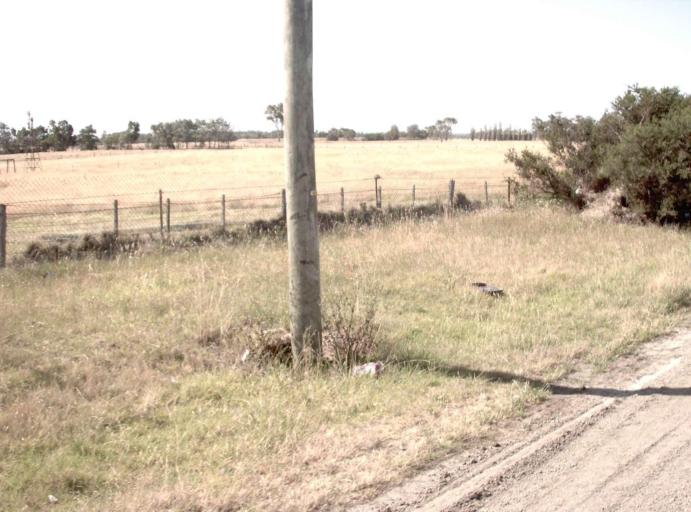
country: AU
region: Victoria
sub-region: Frankston
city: Carrum Downs
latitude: -38.0830
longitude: 145.1856
